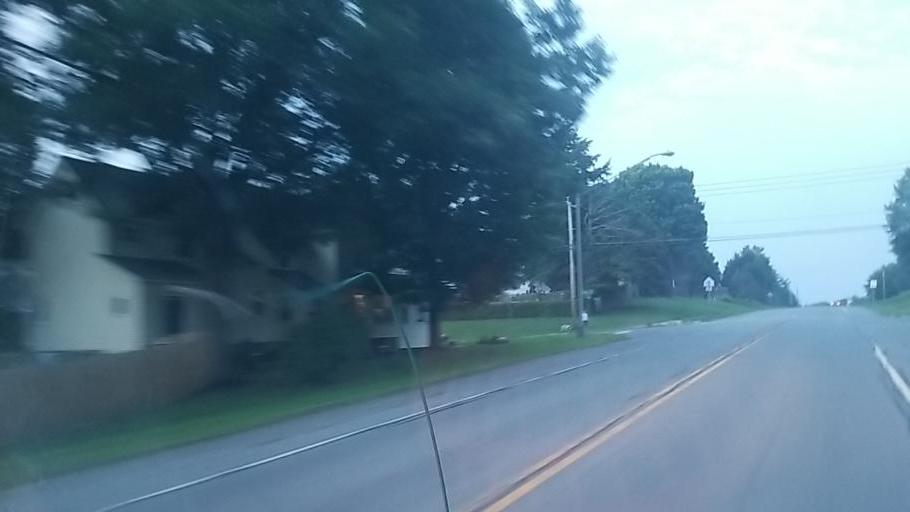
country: US
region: New York
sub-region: Fulton County
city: Johnstown
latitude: 42.9957
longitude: -74.3676
